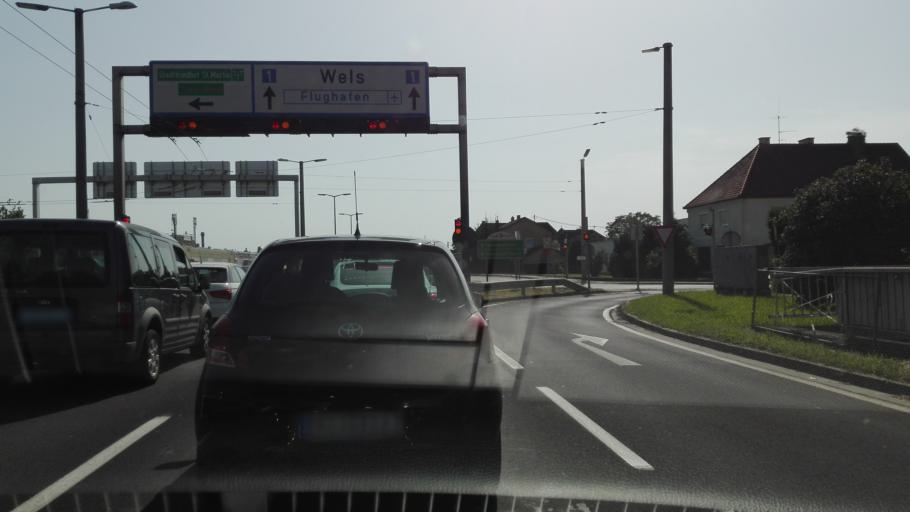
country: AT
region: Upper Austria
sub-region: Politischer Bezirk Linz-Land
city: Traun
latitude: 48.2392
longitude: 14.2455
